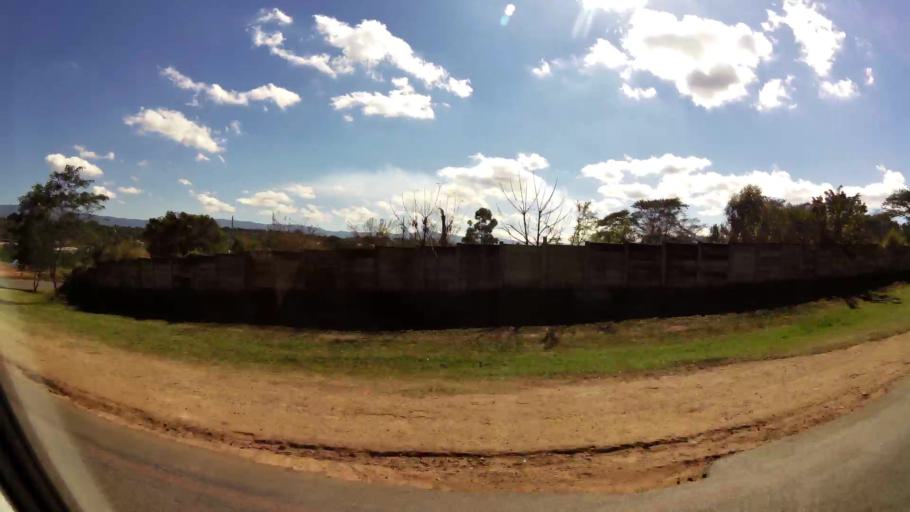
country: ZA
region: Limpopo
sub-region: Mopani District Municipality
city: Tzaneen
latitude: -23.8228
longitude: 30.1676
